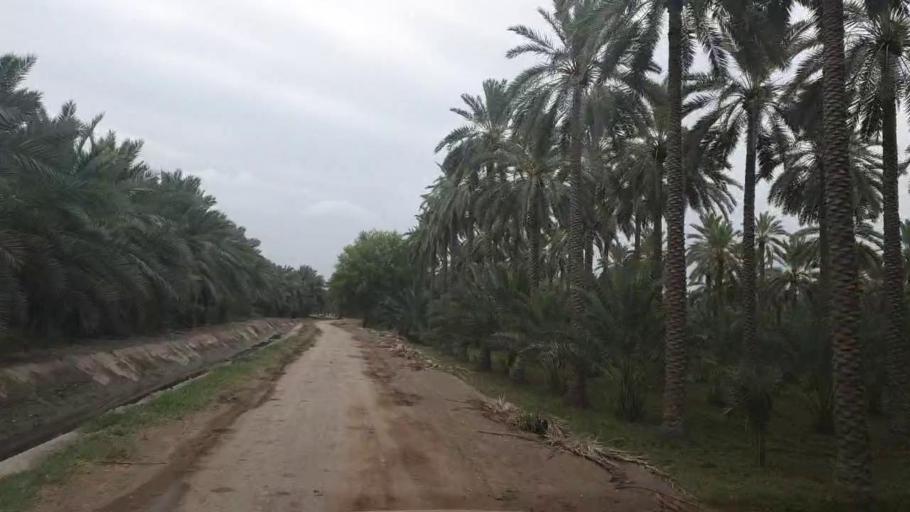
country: PK
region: Sindh
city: Khairpur
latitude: 27.5966
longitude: 68.8007
